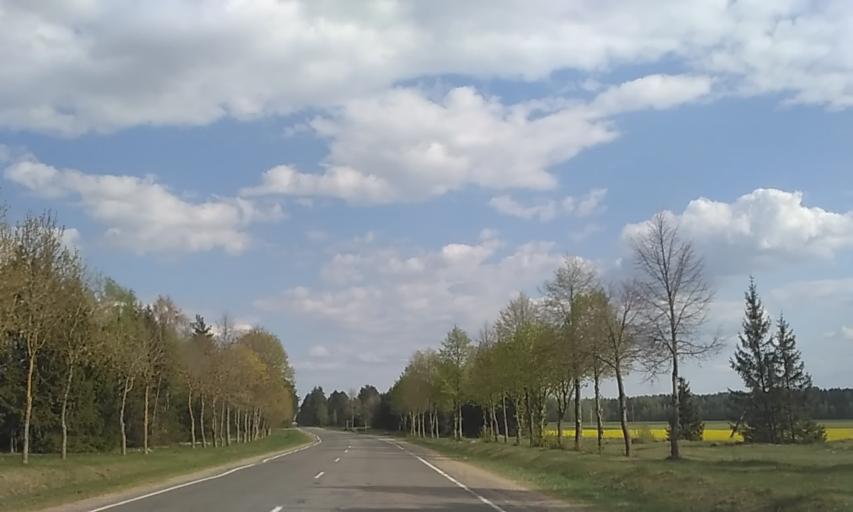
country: BY
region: Minsk
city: Narach
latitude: 54.9526
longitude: 26.6588
